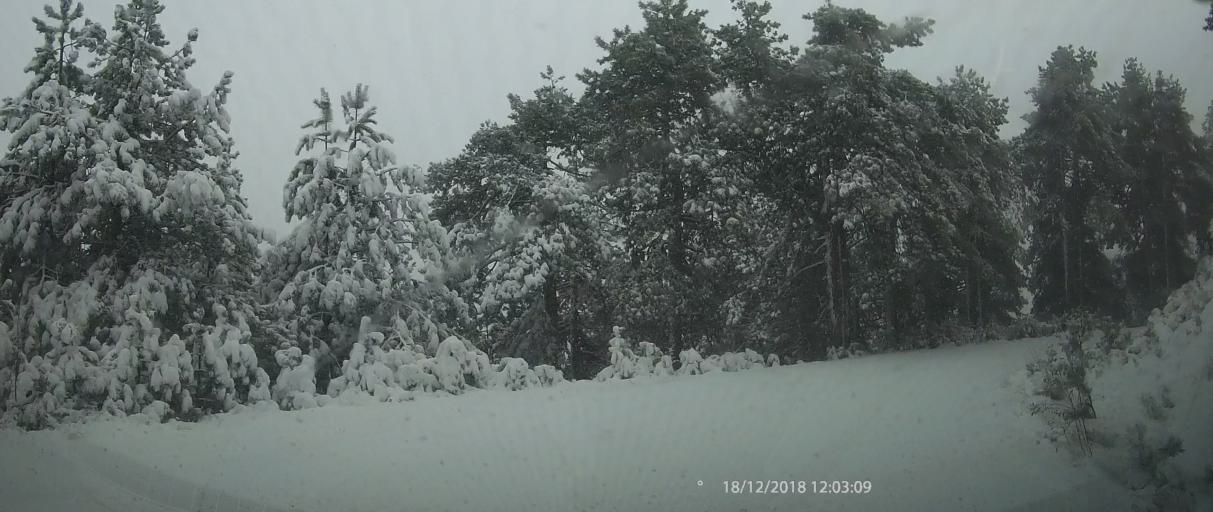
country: GR
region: Central Macedonia
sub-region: Nomos Pierias
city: Litochoro
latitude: 40.1076
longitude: 22.4653
